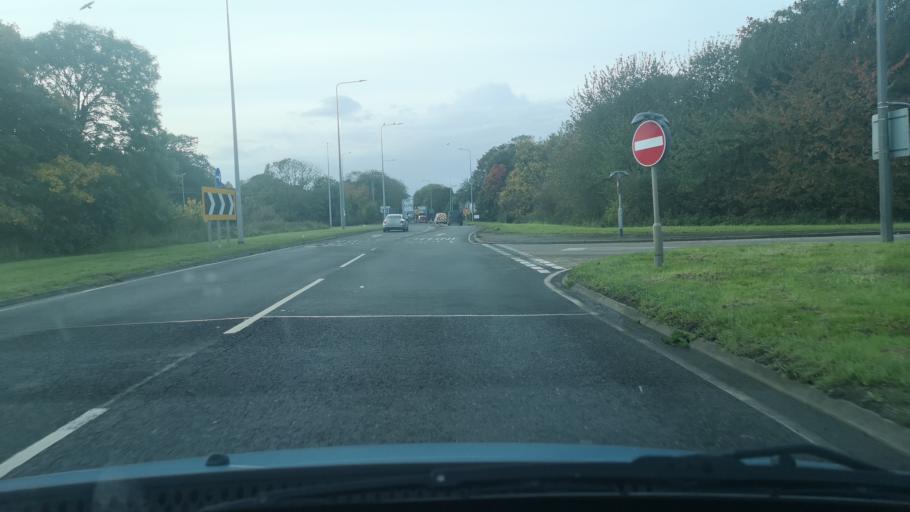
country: GB
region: England
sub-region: North Lincolnshire
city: Crowle
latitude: 53.5852
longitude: -0.8174
